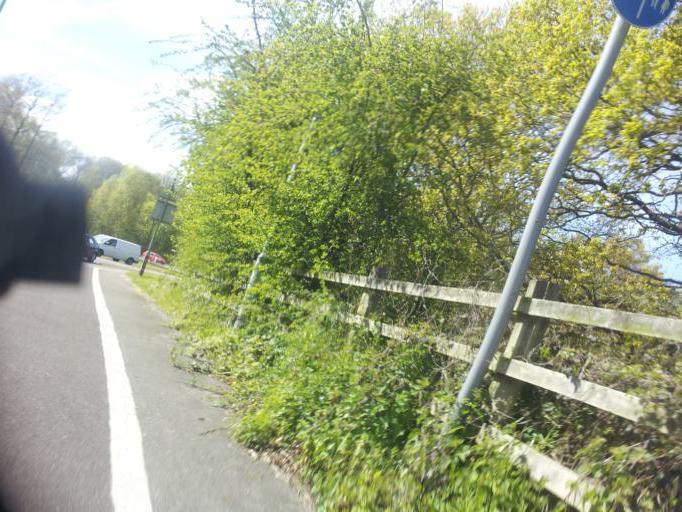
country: GB
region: England
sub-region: Kent
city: Rainham
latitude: 51.3591
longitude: 0.5801
